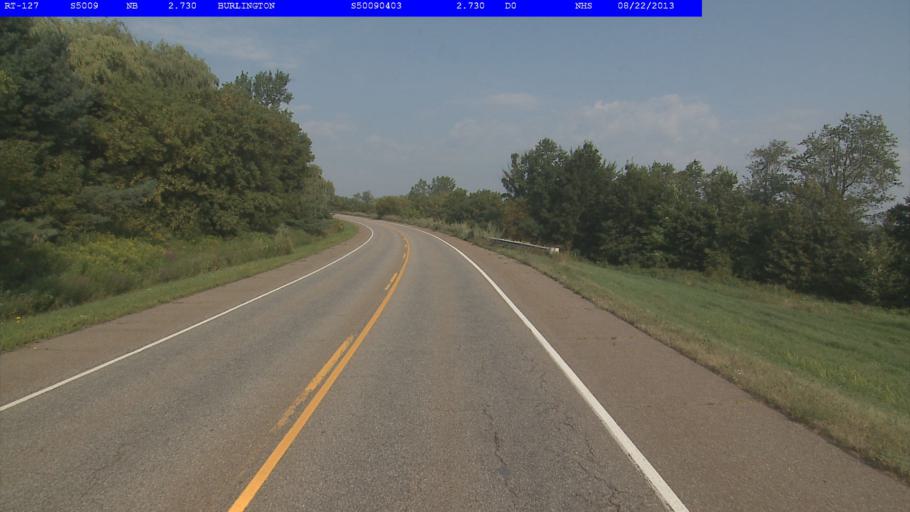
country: US
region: Vermont
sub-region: Chittenden County
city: Burlington
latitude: 44.5205
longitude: -73.2448
